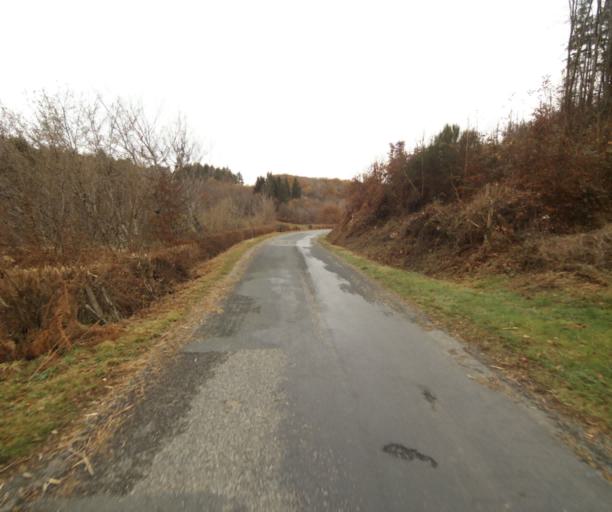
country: FR
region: Limousin
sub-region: Departement de la Correze
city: Sainte-Fortunade
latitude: 45.1815
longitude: 1.7815
